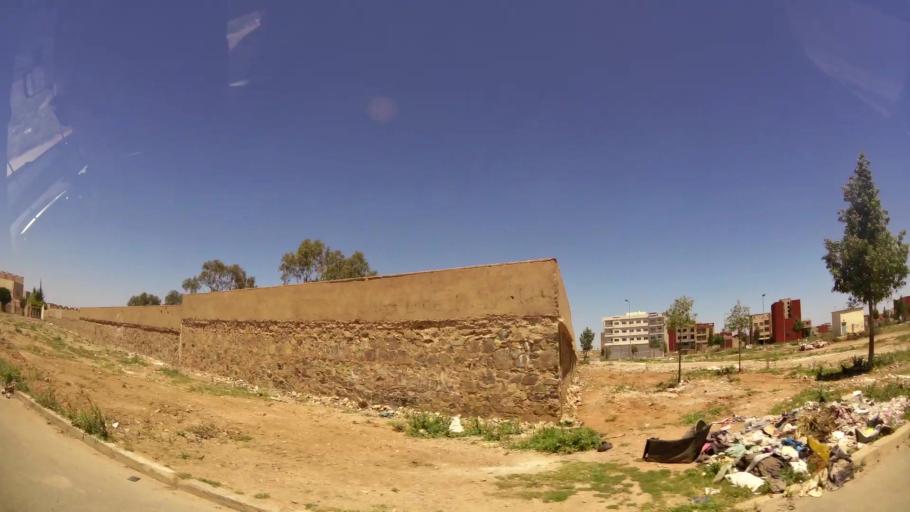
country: MA
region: Oriental
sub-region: Oujda-Angad
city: Oujda
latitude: 34.6684
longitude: -1.8806
